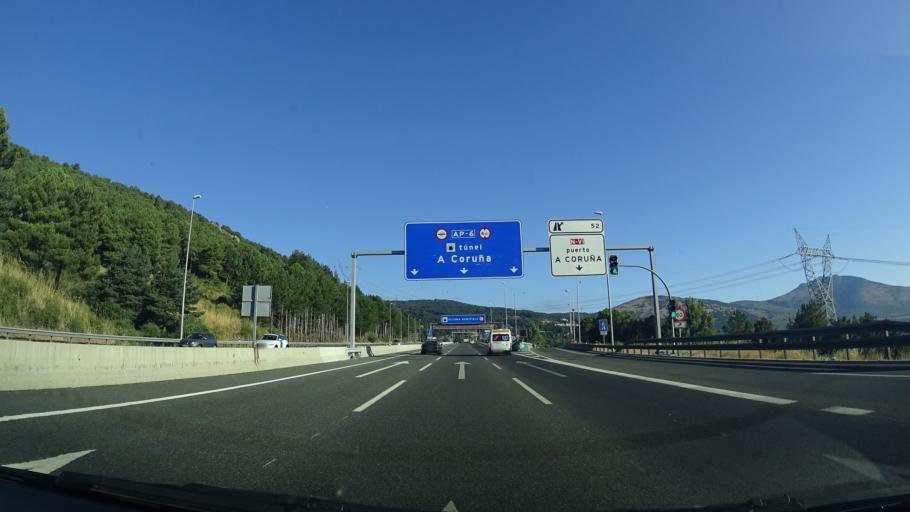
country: ES
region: Madrid
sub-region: Provincia de Madrid
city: Guadarrama
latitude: 40.6909
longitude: -4.1227
